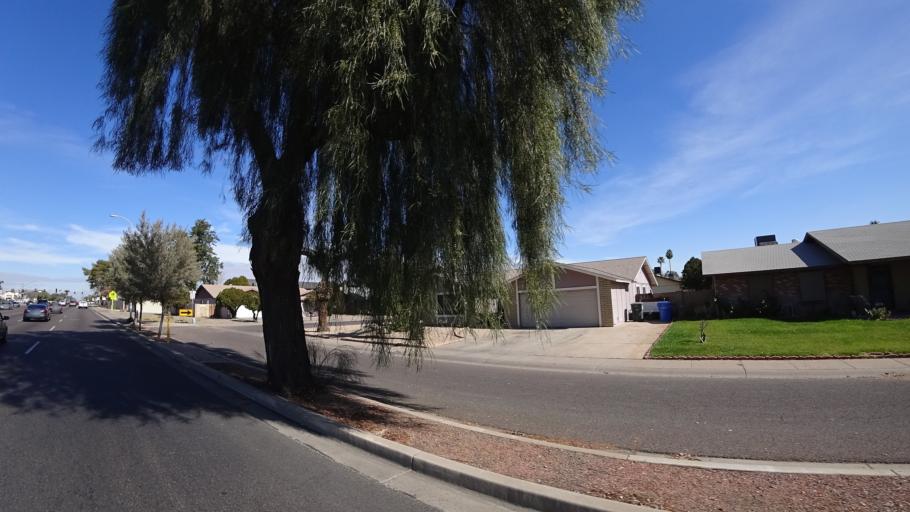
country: US
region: Arizona
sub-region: Maricopa County
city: Glendale
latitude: 33.5071
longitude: -112.2031
